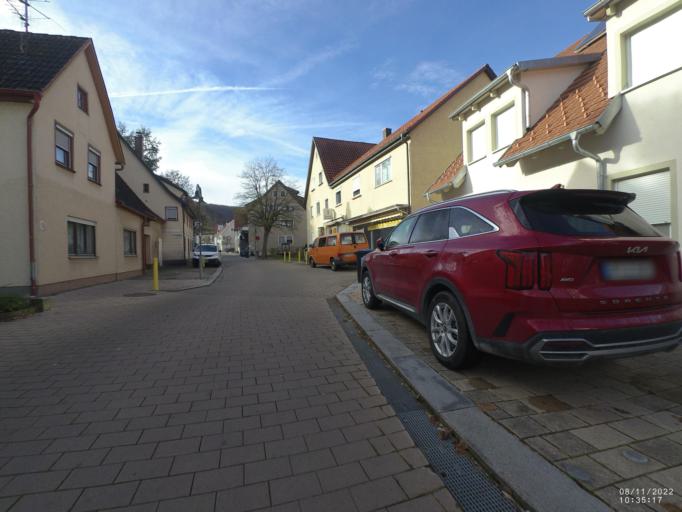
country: DE
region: Baden-Wuerttemberg
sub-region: Regierungsbezirk Stuttgart
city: Bad Ditzenbach
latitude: 48.5877
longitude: 9.7044
